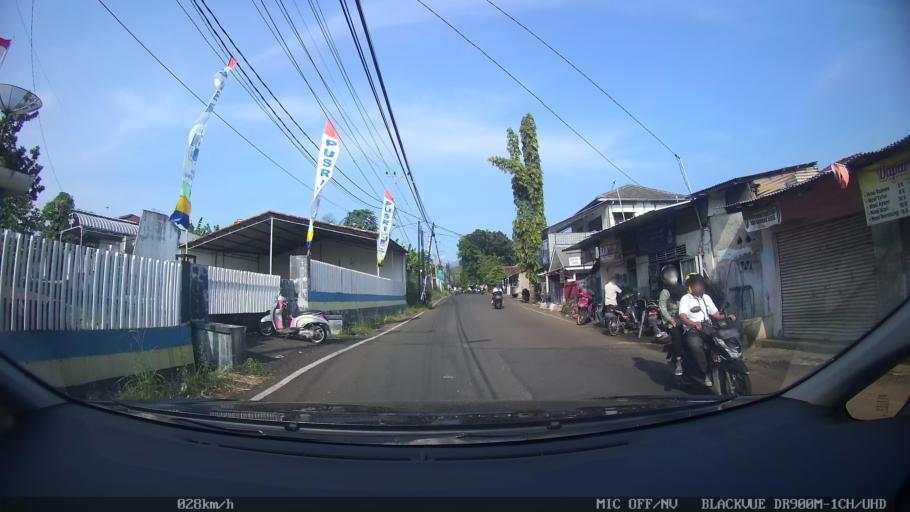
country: ID
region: Lampung
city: Bandarlampung
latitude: -5.4253
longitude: 105.2486
